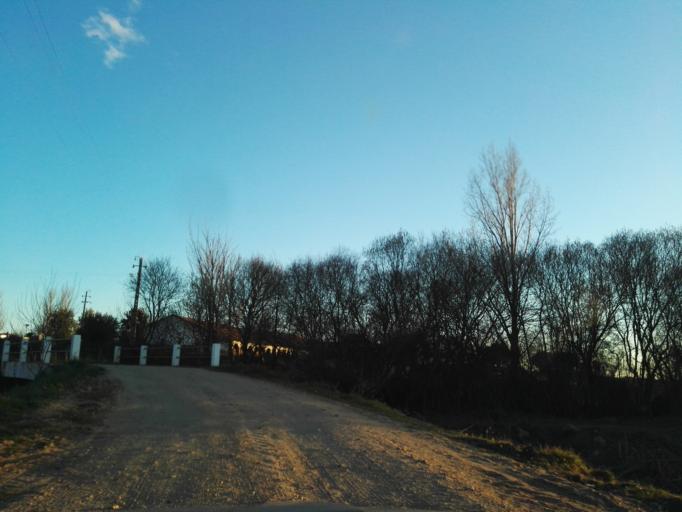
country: PT
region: Castelo Branco
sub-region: Idanha-A-Nova
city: Idanha-a-Nova
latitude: 39.8640
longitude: -7.1352
